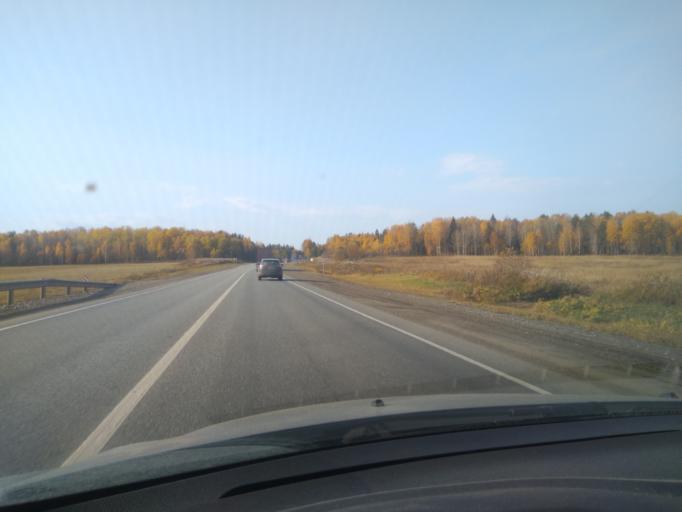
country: RU
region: Sverdlovsk
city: Druzhinino
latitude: 56.8017
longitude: 59.4738
